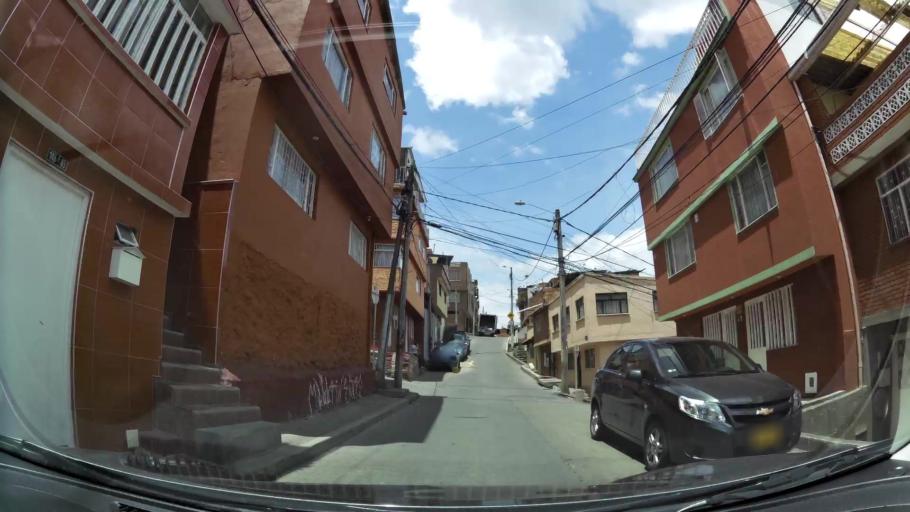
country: CO
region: Cundinamarca
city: Cota
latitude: 4.7384
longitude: -74.0750
